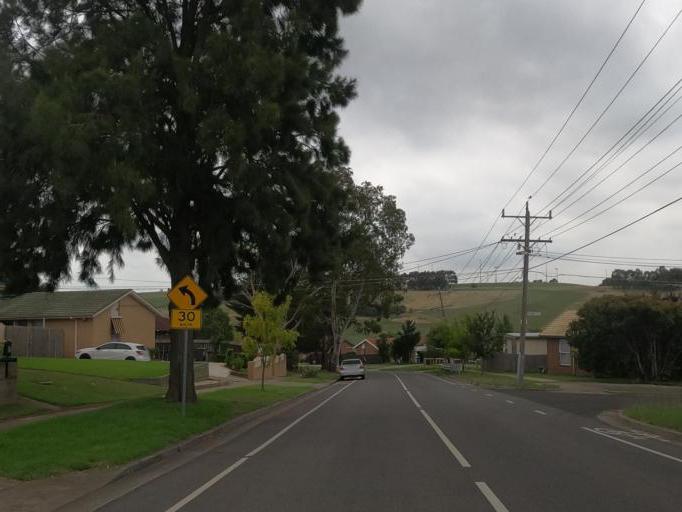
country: AU
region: Victoria
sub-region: Hume
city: Broadmeadows
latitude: -37.6714
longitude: 144.9098
